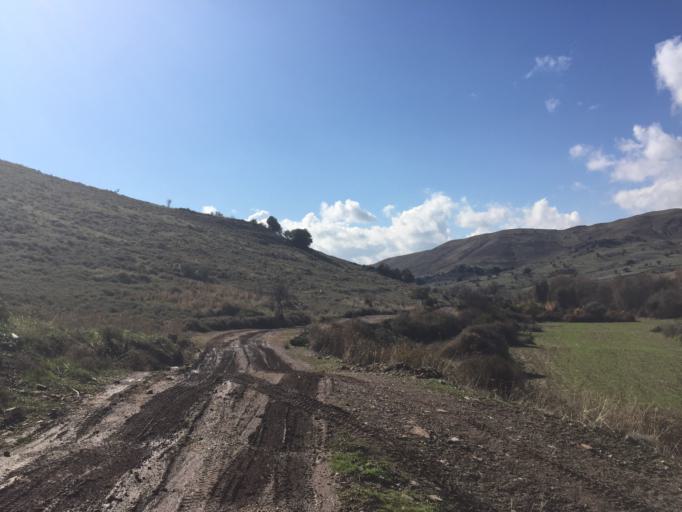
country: CY
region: Limassol
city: Pachna
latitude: 34.8739
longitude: 32.6729
